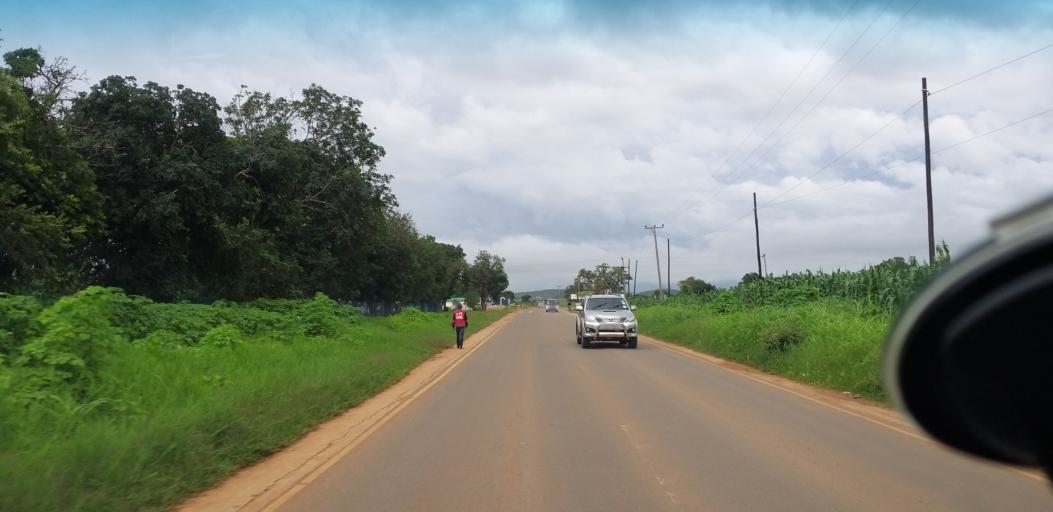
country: ZM
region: Lusaka
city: Lusaka
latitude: -15.5193
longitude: 28.2976
